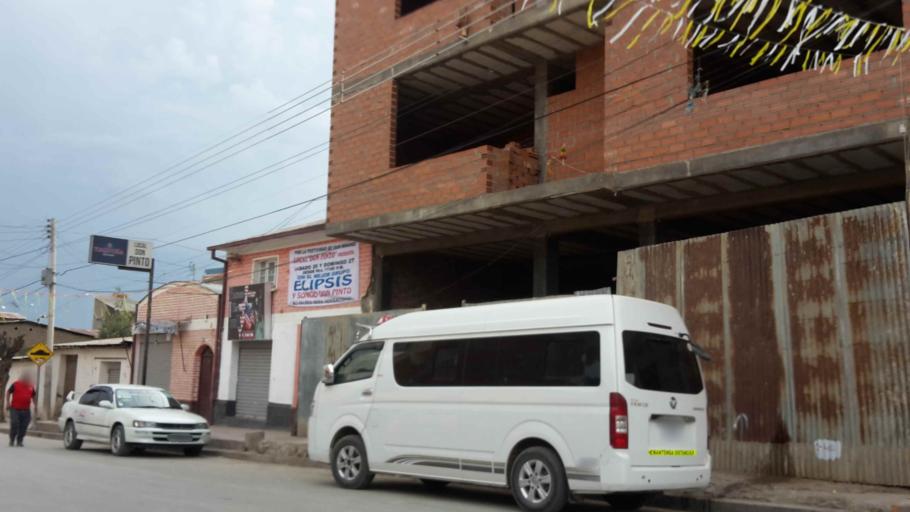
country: BO
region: Cochabamba
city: Cochabamba
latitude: -17.3379
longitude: -66.2211
